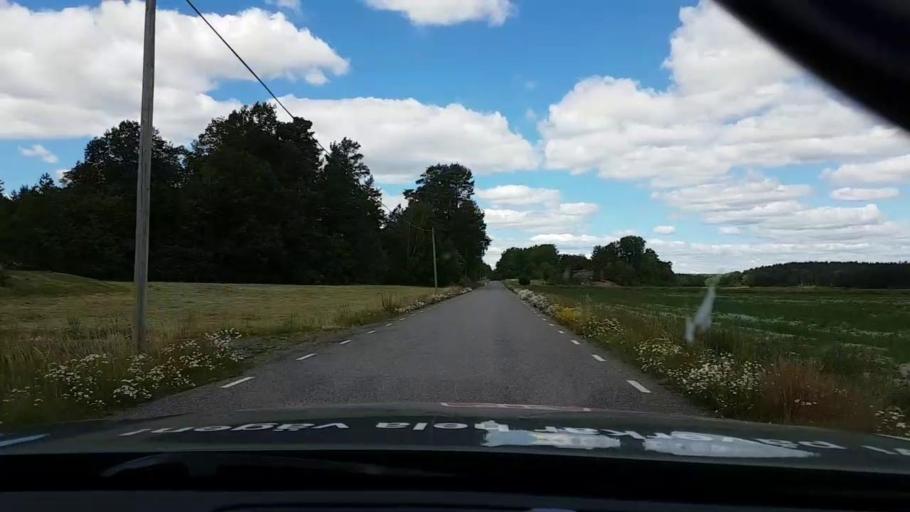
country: SE
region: Kalmar
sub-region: Vasterviks Kommun
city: Forserum
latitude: 57.9917
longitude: 16.6025
